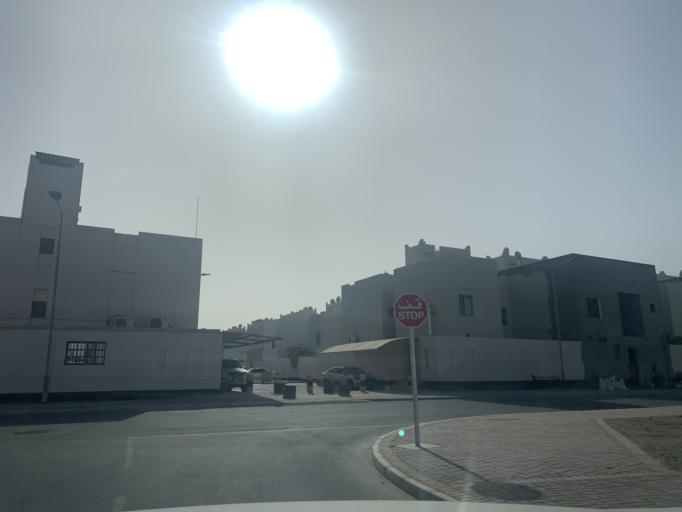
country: BH
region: Northern
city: Sitrah
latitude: 26.1597
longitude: 50.6251
